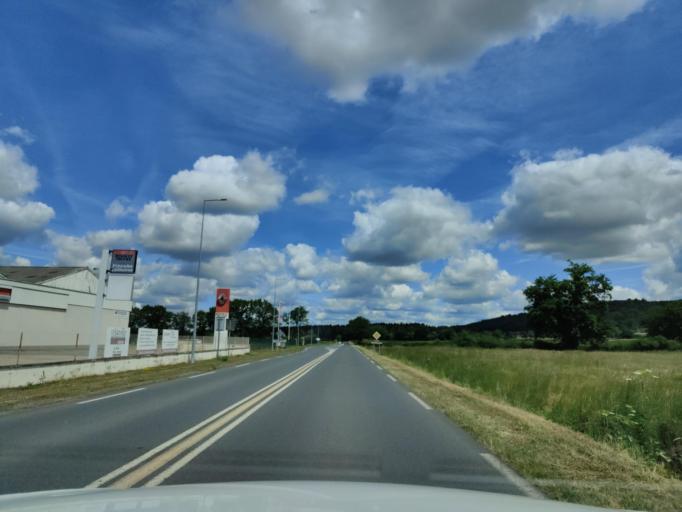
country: FR
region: Auvergne
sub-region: Departement de l'Allier
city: Estivareilles
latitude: 46.4286
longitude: 2.6137
